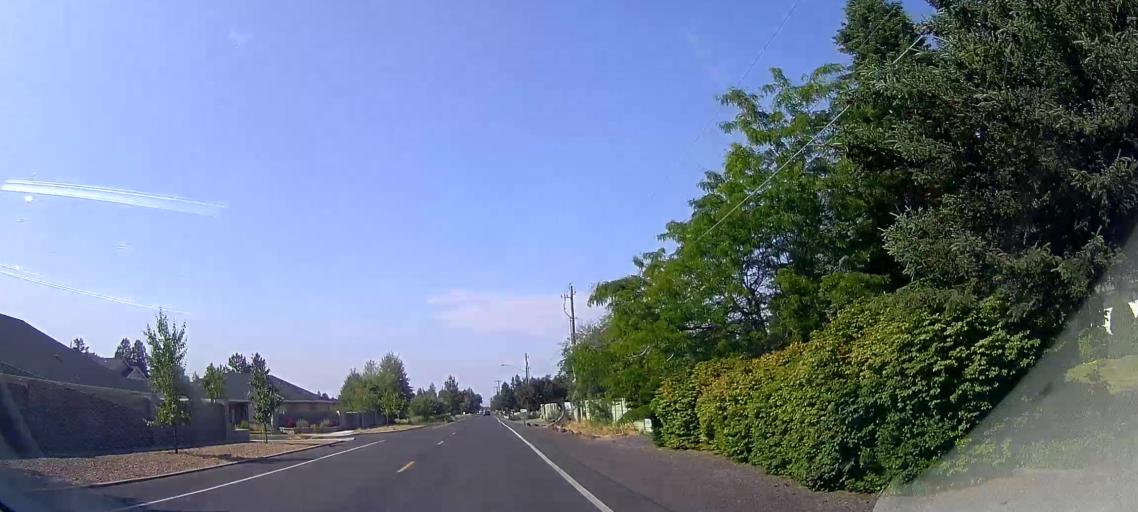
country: US
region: Oregon
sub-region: Deschutes County
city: Bend
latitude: 44.0456
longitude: -121.2686
